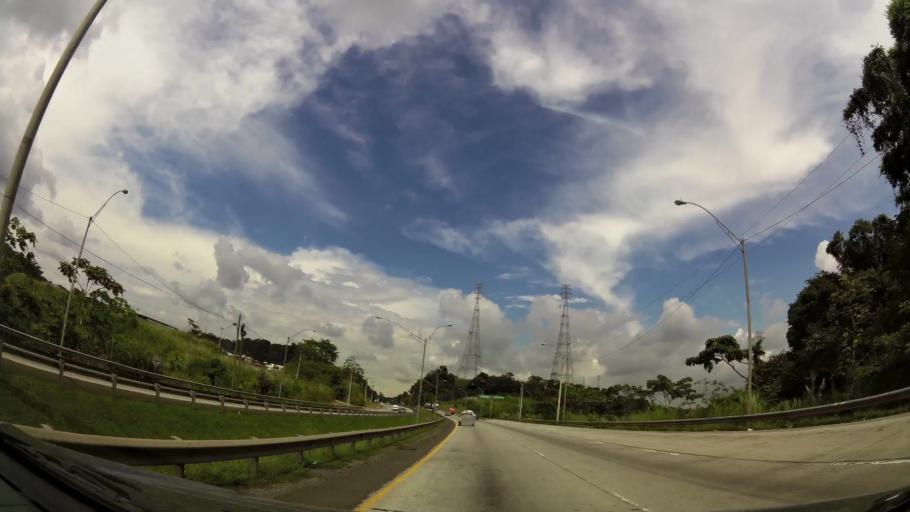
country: PA
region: Panama
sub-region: Distrito de Panama
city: Paraiso
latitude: 9.0209
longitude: -79.6397
